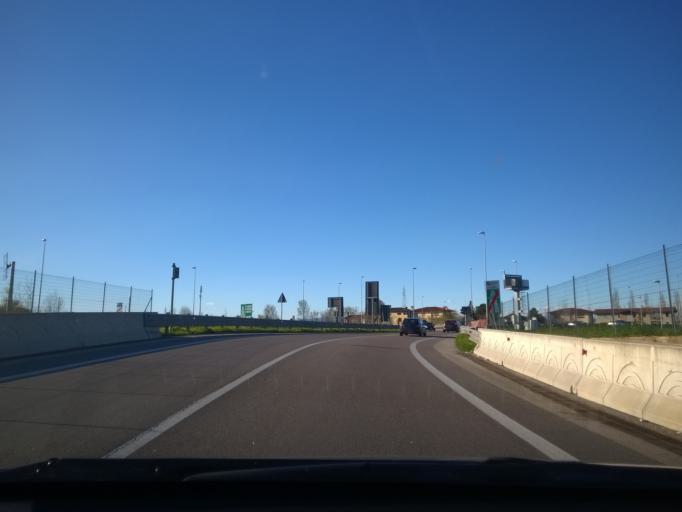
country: IT
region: Veneto
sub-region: Provincia di Venezia
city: Marano
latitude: 45.4629
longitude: 12.1079
